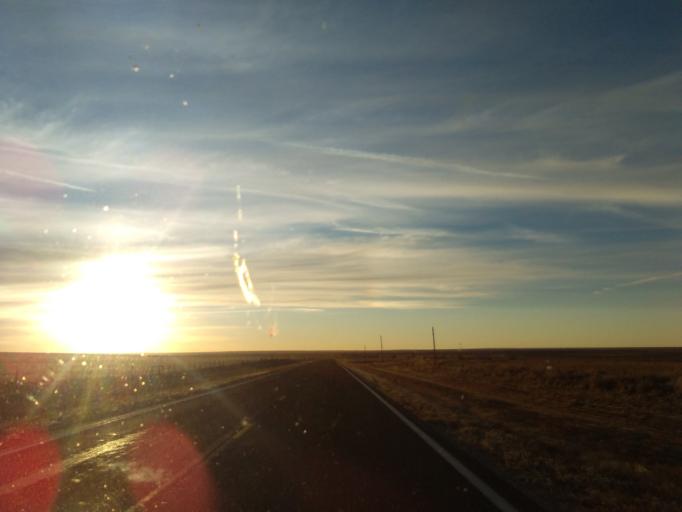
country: US
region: Kansas
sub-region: Wallace County
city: Sharon Springs
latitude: 39.0058
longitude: -101.3800
